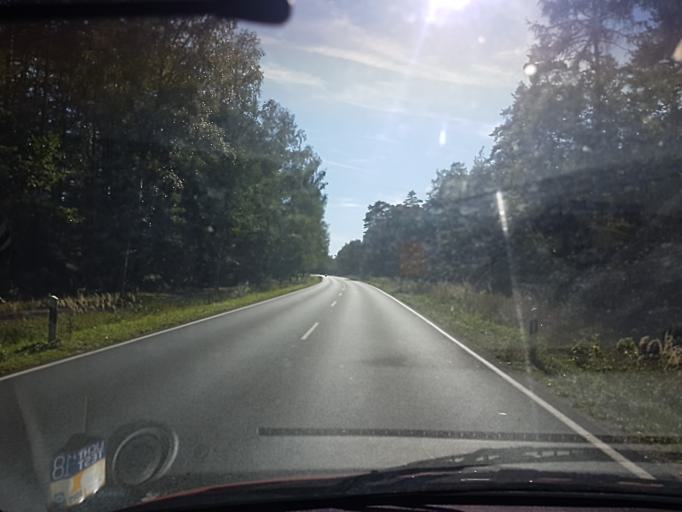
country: DE
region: Bavaria
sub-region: Regierungsbezirk Mittelfranken
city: Hemhofen
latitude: 49.7025
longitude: 10.9512
